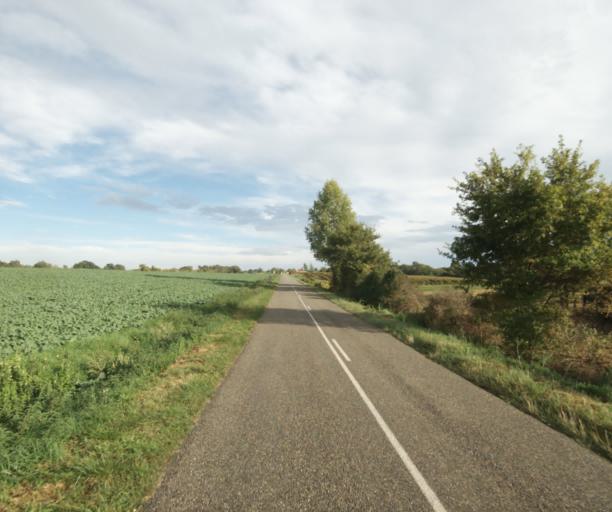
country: FR
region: Midi-Pyrenees
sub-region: Departement du Gers
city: Le Houga
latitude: 43.8616
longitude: -0.1532
